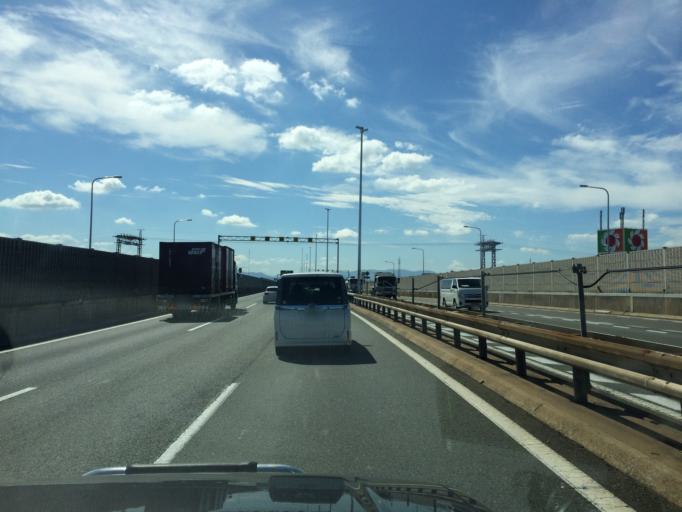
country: JP
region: Osaka
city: Matsubara
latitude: 34.5766
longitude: 135.5632
